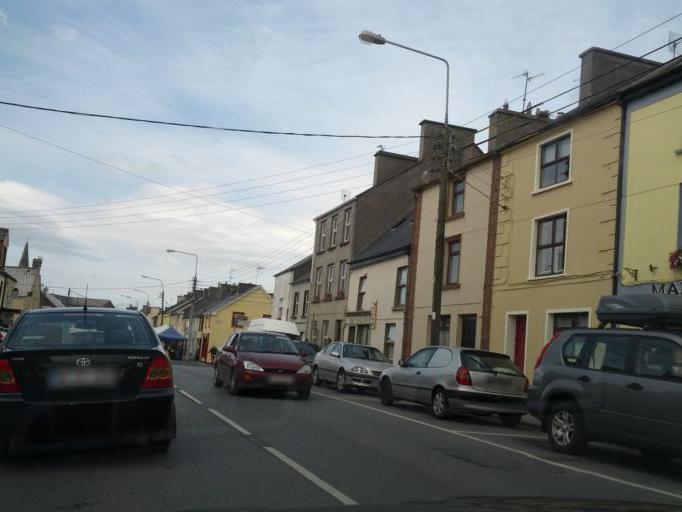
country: IE
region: Munster
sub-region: An Clar
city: Kilrush
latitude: 52.8558
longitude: -9.4009
